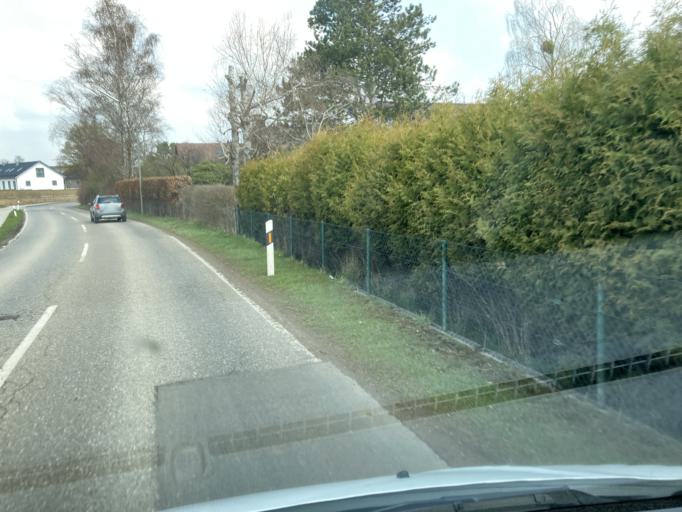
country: DE
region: Bavaria
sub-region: Upper Bavaria
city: Grafing bei Munchen
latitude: 48.0382
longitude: 11.9587
